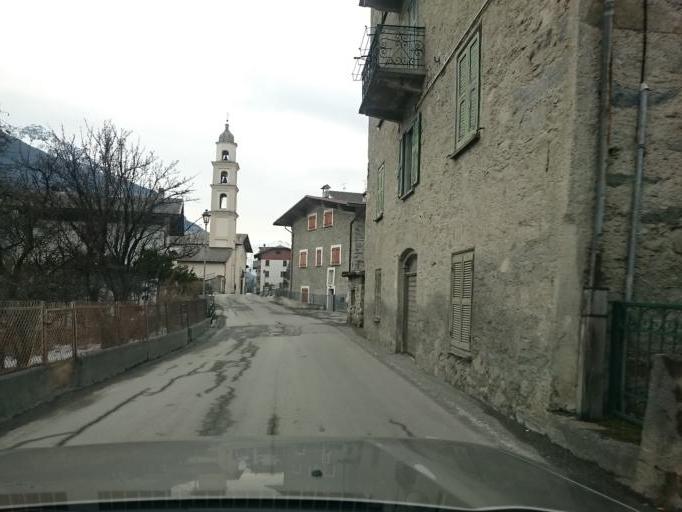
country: IT
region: Lombardy
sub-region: Provincia di Sondrio
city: Bormio
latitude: 46.4580
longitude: 10.3574
